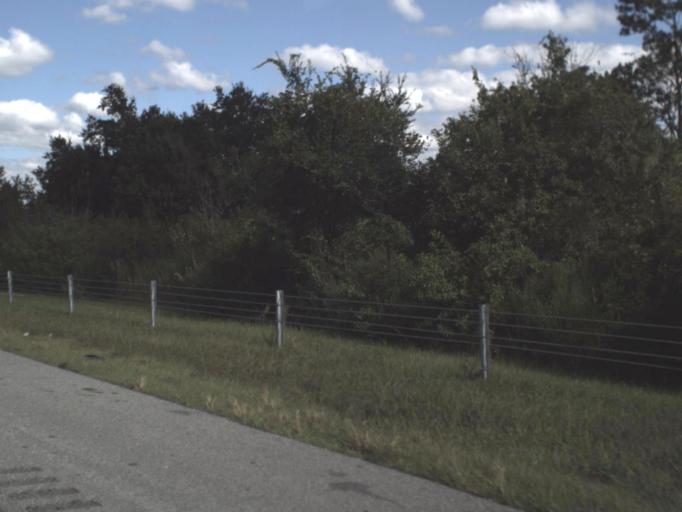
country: US
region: Florida
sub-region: Osceola County
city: Saint Cloud
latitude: 28.1925
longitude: -81.3049
